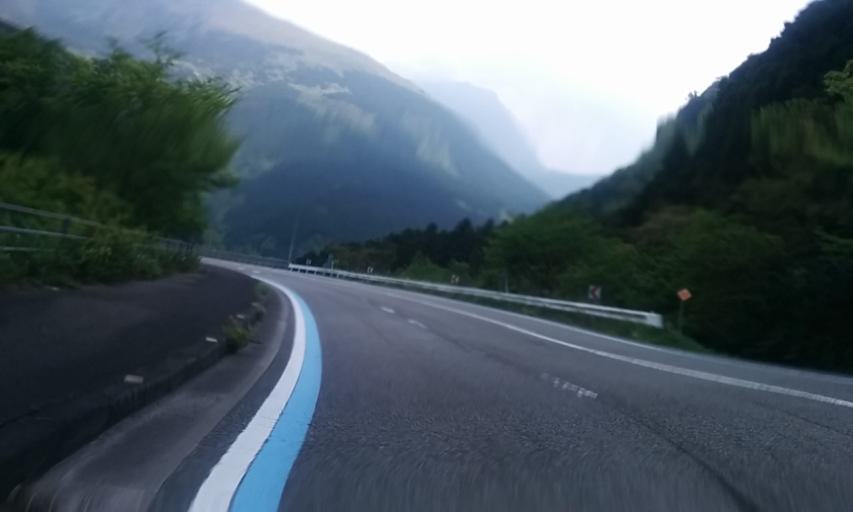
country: JP
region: Ehime
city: Saijo
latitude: 33.8333
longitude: 133.2261
